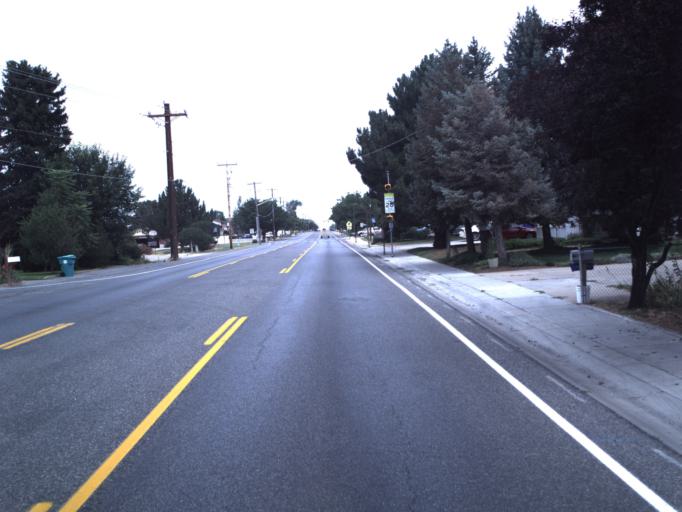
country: US
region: Utah
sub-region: Davis County
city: West Point
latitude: 41.1202
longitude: -112.0645
